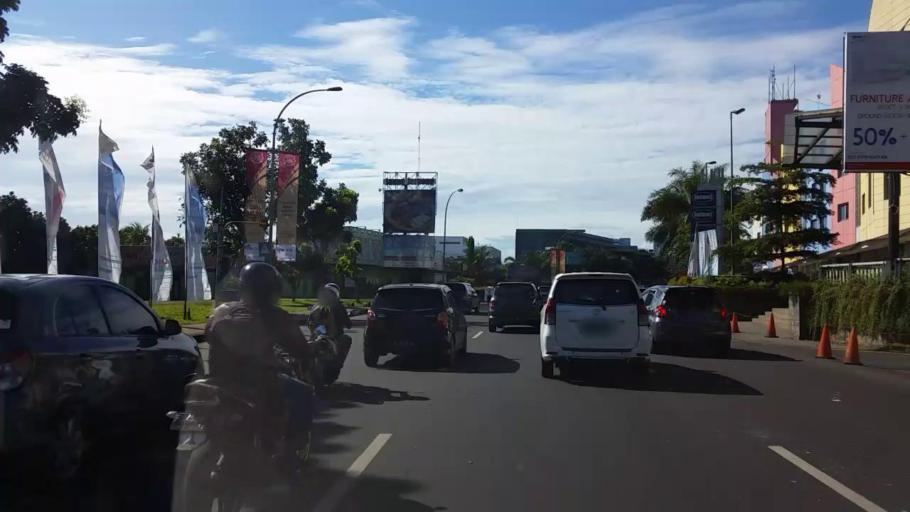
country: ID
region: West Java
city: Serpong
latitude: -6.2846
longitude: 106.6658
